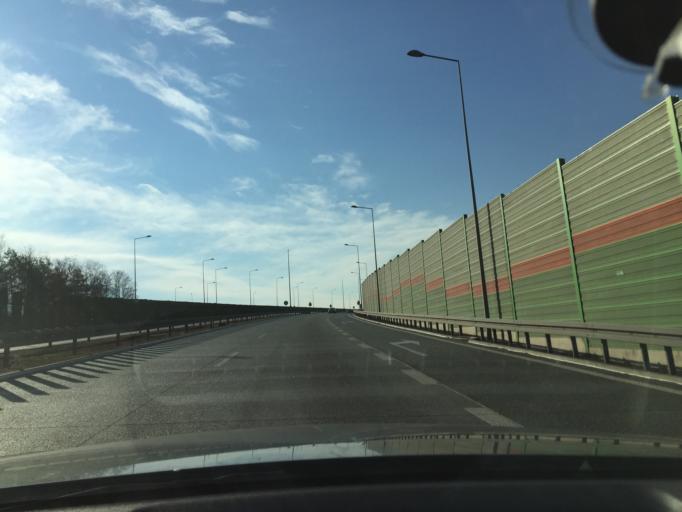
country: PL
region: Lodz Voivodeship
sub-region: Powiat rawski
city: Rawa Mazowiecka
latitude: 51.7067
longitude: 20.2200
